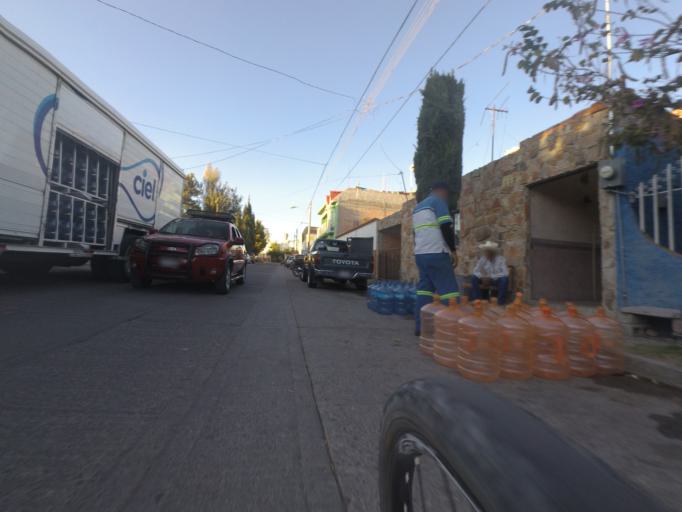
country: MX
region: Aguascalientes
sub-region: Aguascalientes
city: La Loma de los Negritos
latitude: 21.8547
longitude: -102.3398
